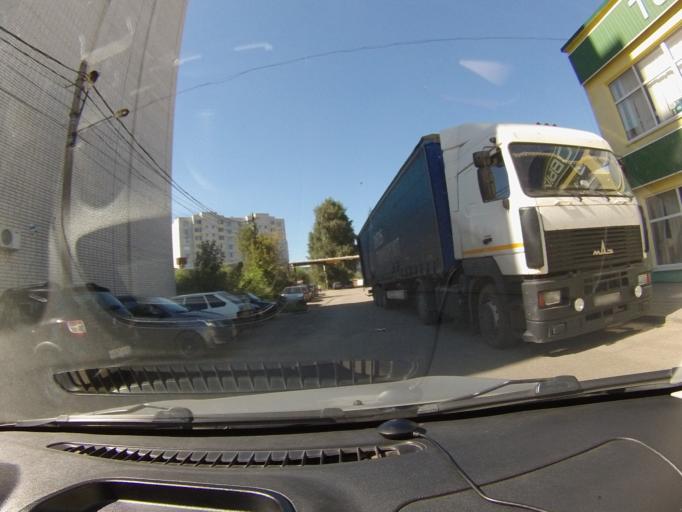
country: RU
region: Tambov
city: Tambov
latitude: 52.7593
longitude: 41.4336
